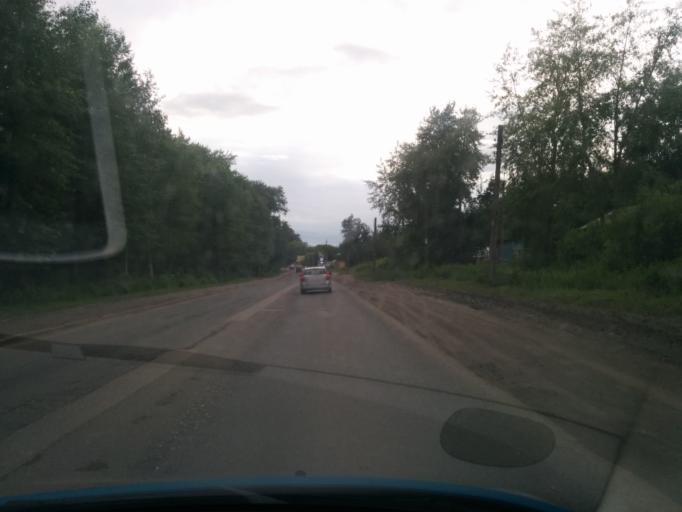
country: RU
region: Perm
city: Perm
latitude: 58.0031
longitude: 56.1880
